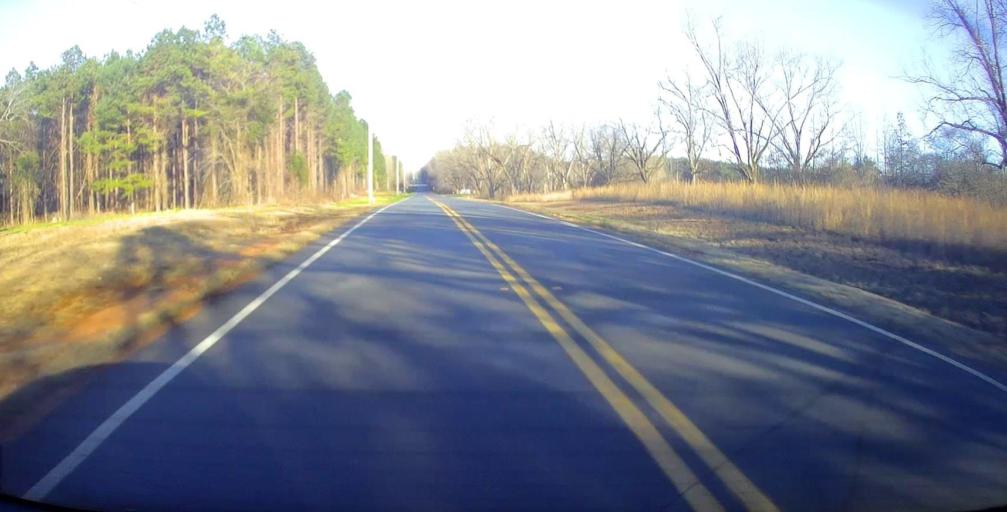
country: US
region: Georgia
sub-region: Harris County
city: Pine Mountain
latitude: 32.9162
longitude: -84.7881
